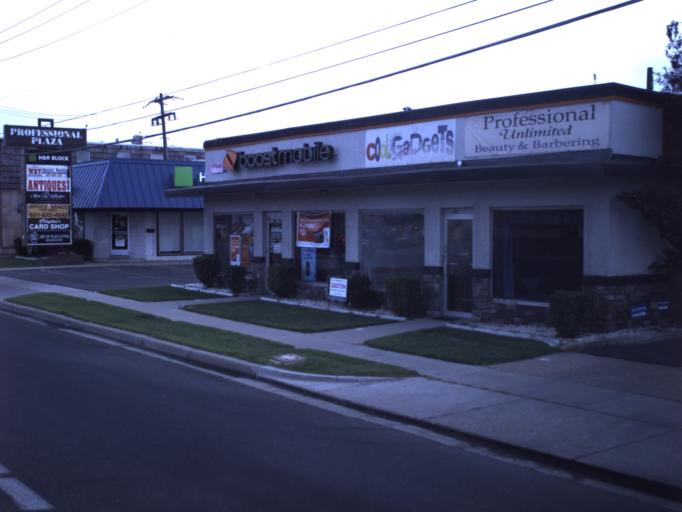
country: US
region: Utah
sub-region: Weber County
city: Roy
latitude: 41.1635
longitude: -112.0261
